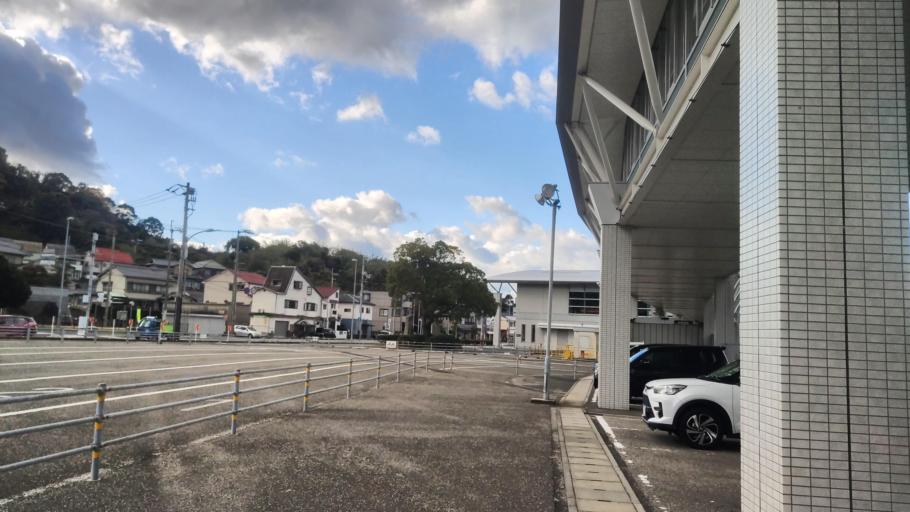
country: JP
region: Ehime
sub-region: Shikoku-chuo Shi
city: Matsuyama
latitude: 33.8894
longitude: 132.7054
